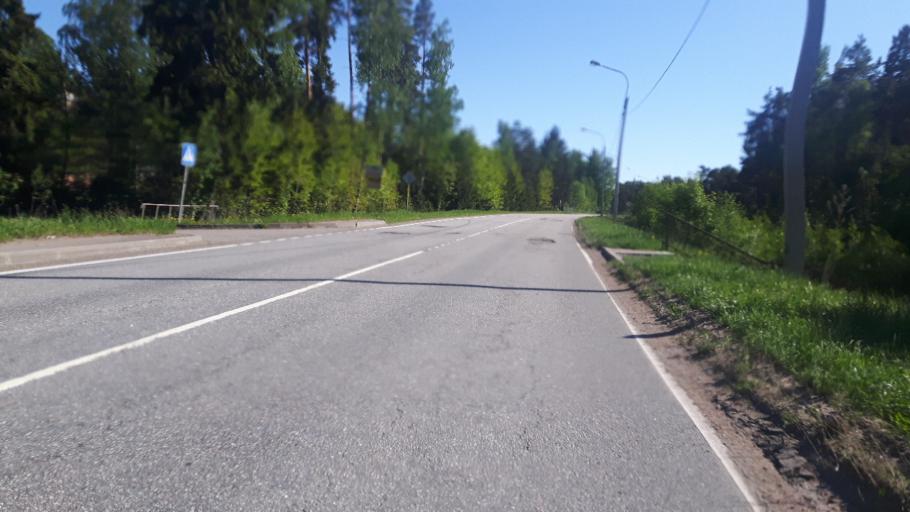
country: RU
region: Leningrad
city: Sosnovyy Bor
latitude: 60.1982
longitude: 29.0072
